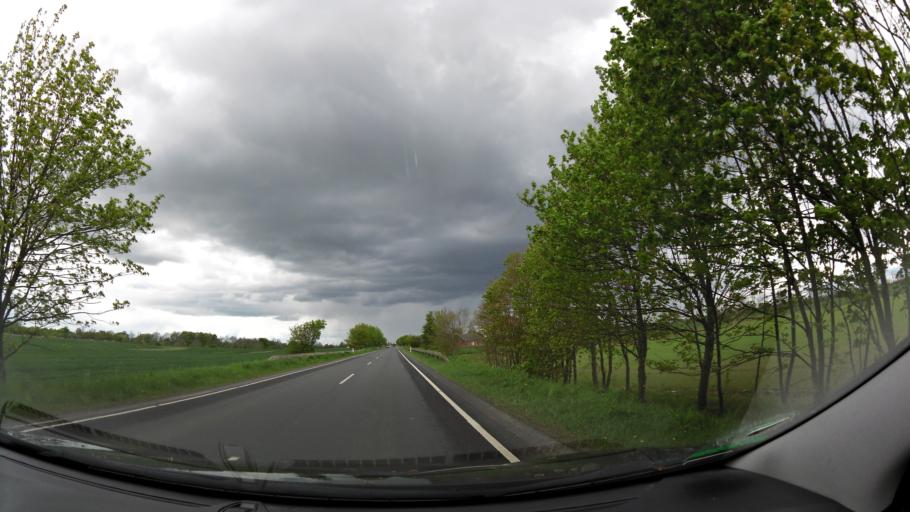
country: DK
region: South Denmark
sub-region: Nyborg Kommune
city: Nyborg
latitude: 55.2103
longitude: 10.7292
